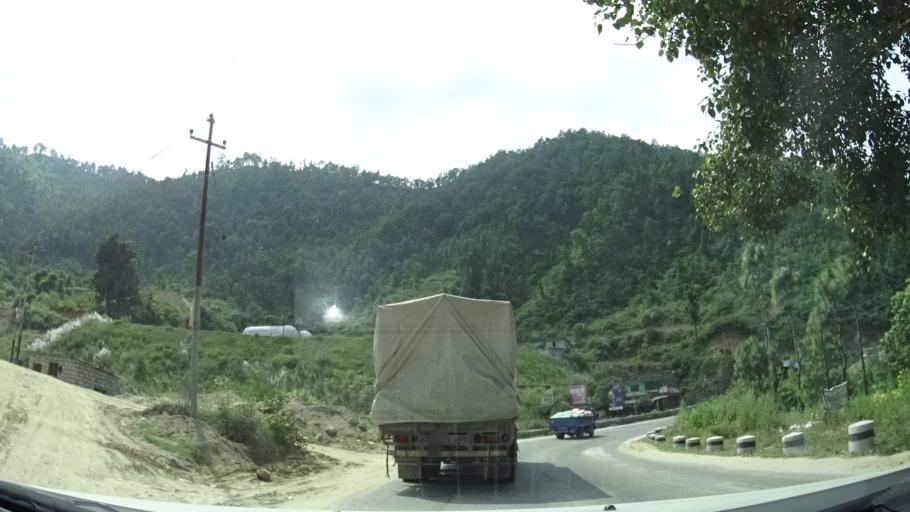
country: NP
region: Central Region
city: Kirtipur
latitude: 27.8005
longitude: 84.9734
